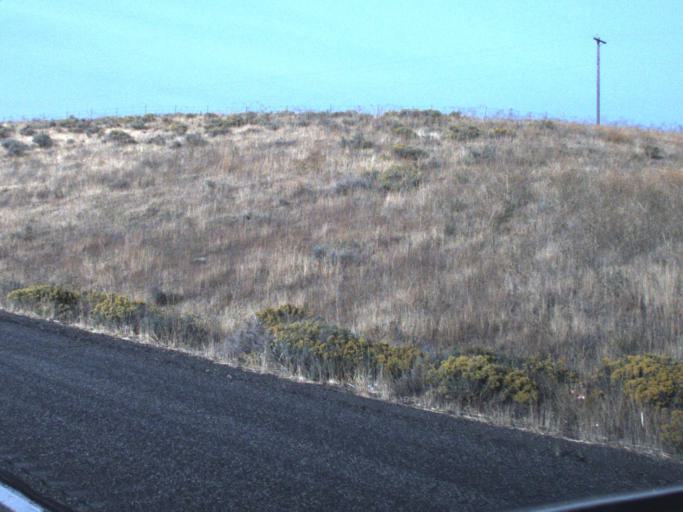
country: US
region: Washington
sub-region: Benton County
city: Highland
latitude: 46.0637
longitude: -119.2232
